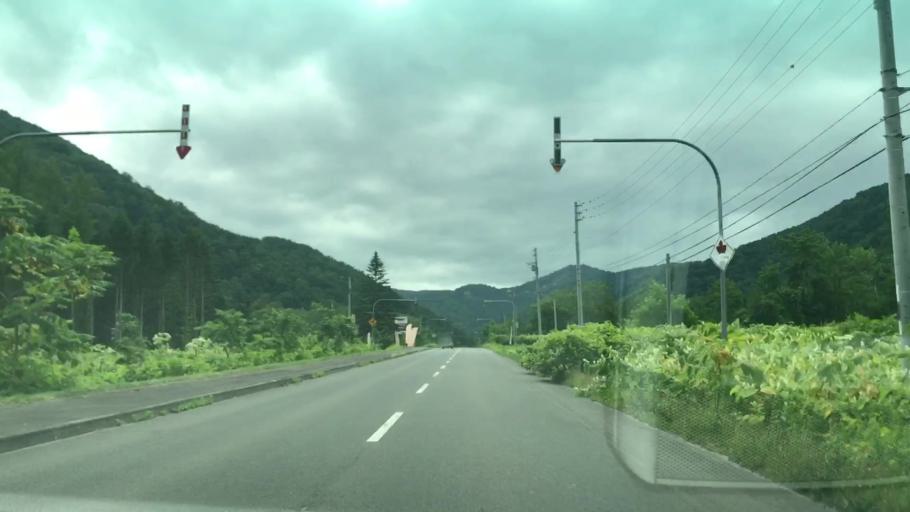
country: JP
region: Hokkaido
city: Yoichi
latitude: 43.0291
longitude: 140.8659
